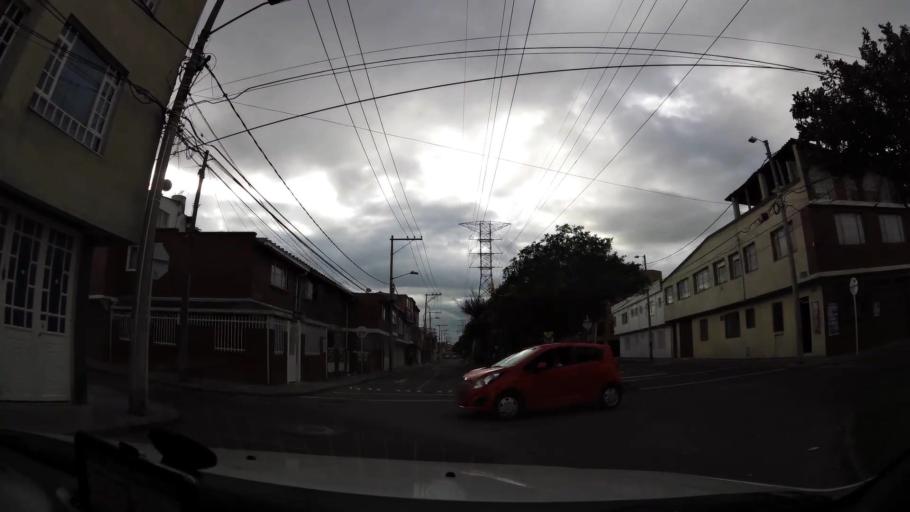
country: CO
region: Bogota D.C.
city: Bogota
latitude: 4.6091
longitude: -74.1096
